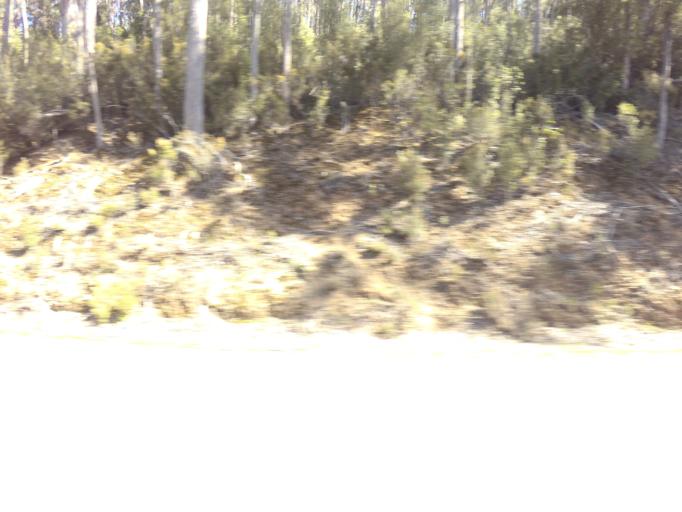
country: AU
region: Tasmania
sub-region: Derwent Valley
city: New Norfolk
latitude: -42.7473
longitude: 146.5031
